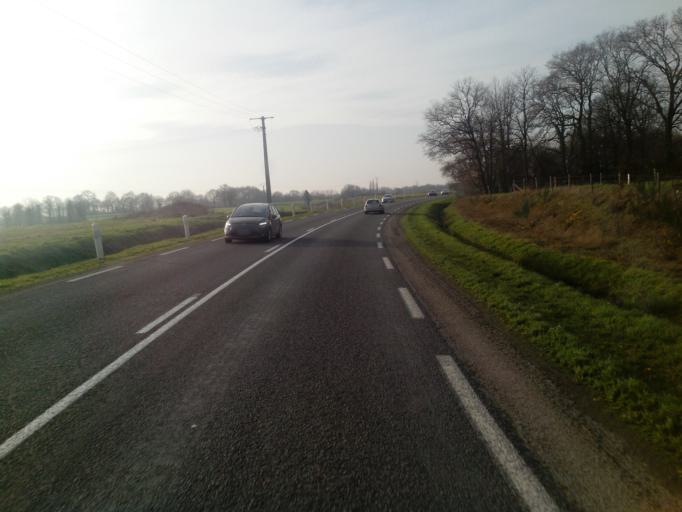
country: FR
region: Brittany
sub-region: Departement d'Ille-et-Vilaine
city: Boisgervilly
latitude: 48.1912
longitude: -2.1209
